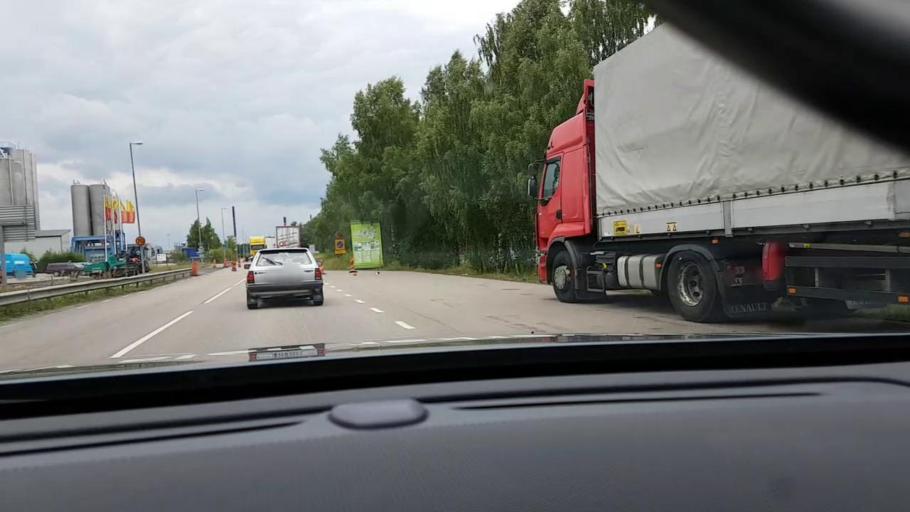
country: SE
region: Skane
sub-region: Hassleholms Kommun
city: Hassleholm
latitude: 56.1563
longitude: 13.8138
